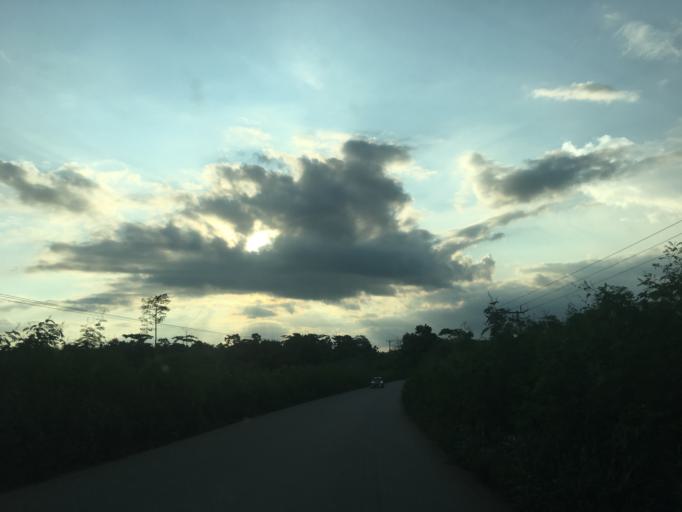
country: GH
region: Western
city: Bibiani
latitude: 6.6335
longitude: -2.4224
